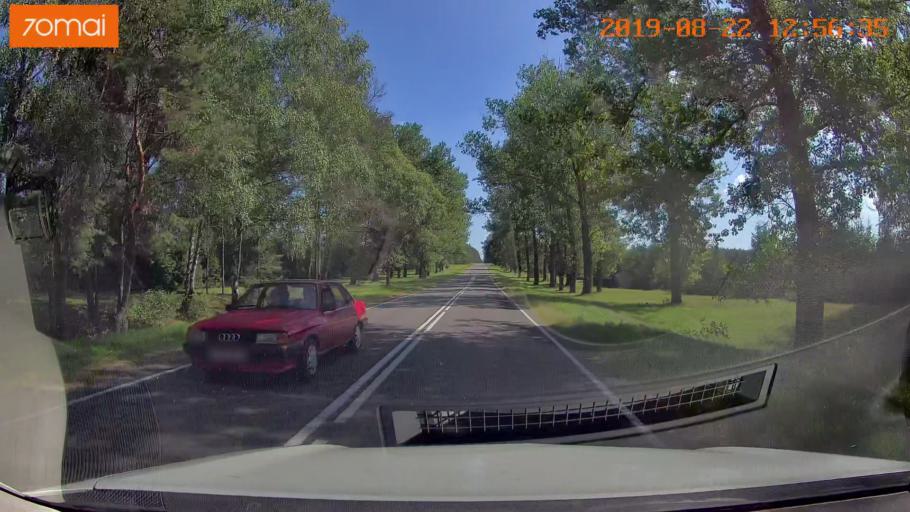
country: BY
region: Minsk
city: Prawdzinski
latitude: 53.4324
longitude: 27.7332
